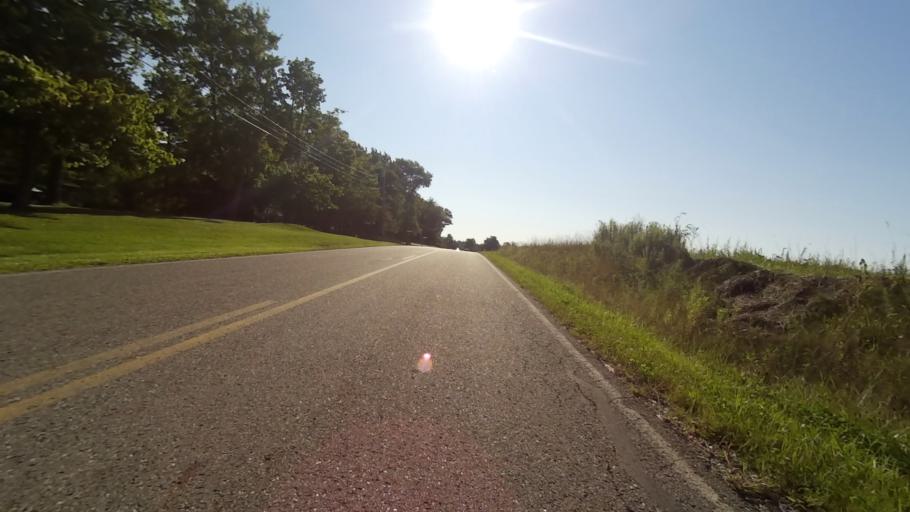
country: US
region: Ohio
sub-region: Portage County
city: Mantua
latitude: 41.2935
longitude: -81.2721
